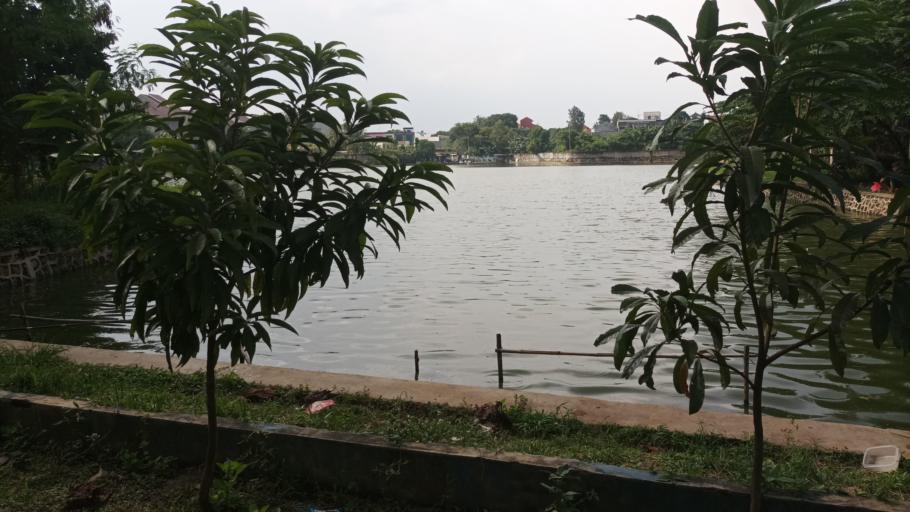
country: ID
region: West Java
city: Depok
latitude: -6.3748
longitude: 106.8682
